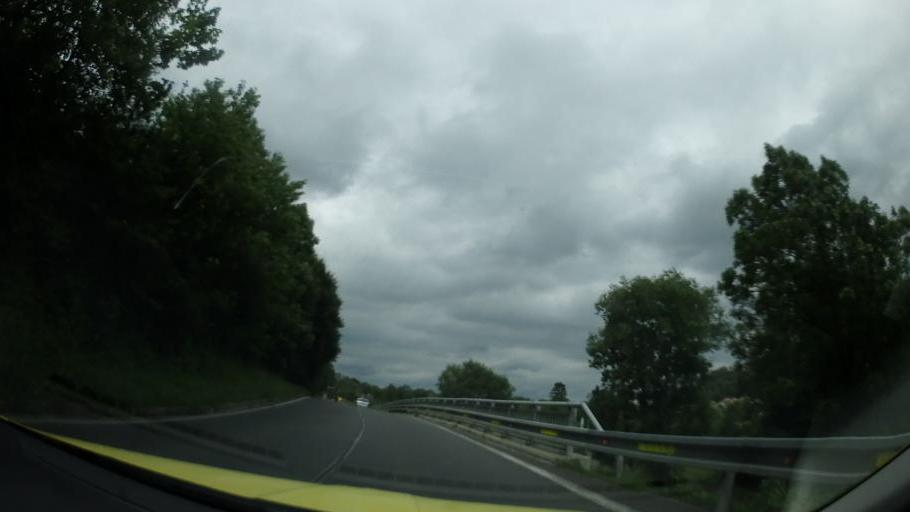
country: CZ
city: Stramberk
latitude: 49.5785
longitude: 18.1263
